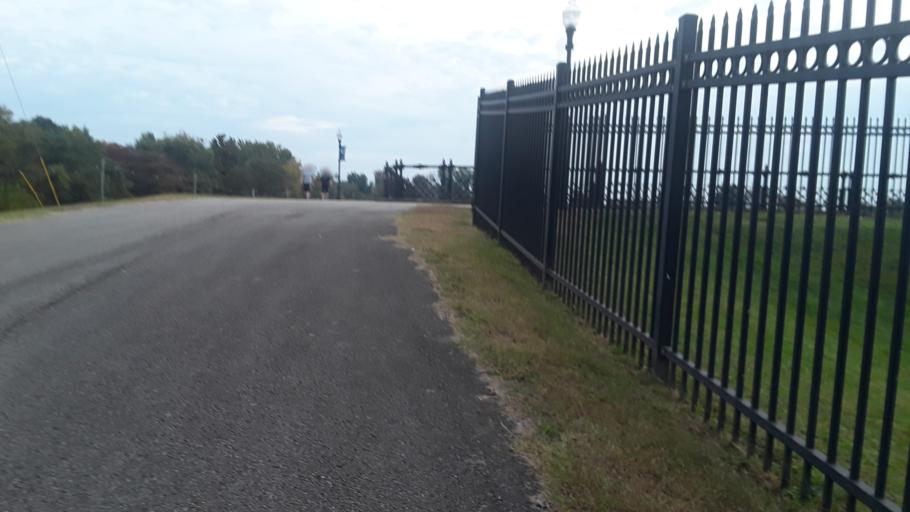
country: US
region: Kentucky
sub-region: Jefferson County
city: Indian Hills
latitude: 38.2586
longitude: -85.6780
